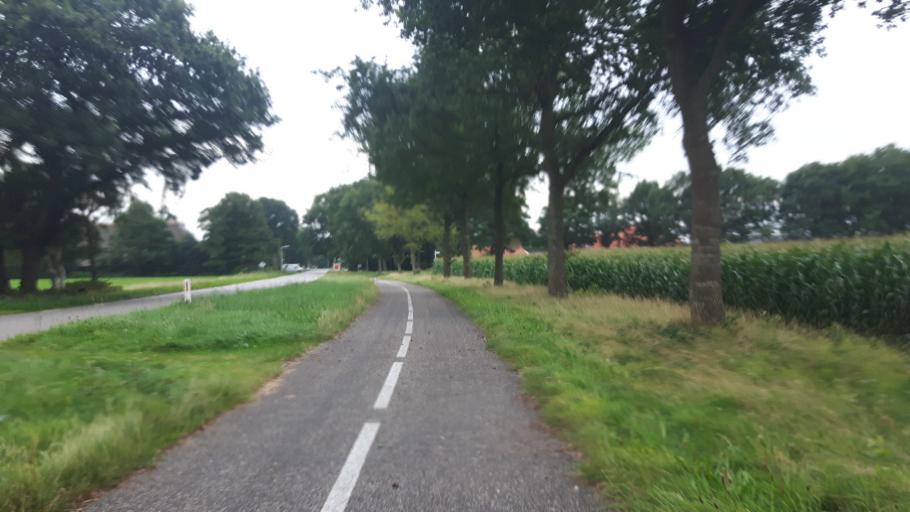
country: NL
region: Friesland
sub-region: Gemeente Weststellingwerf
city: Noordwolde
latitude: 52.9592
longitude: 6.2200
